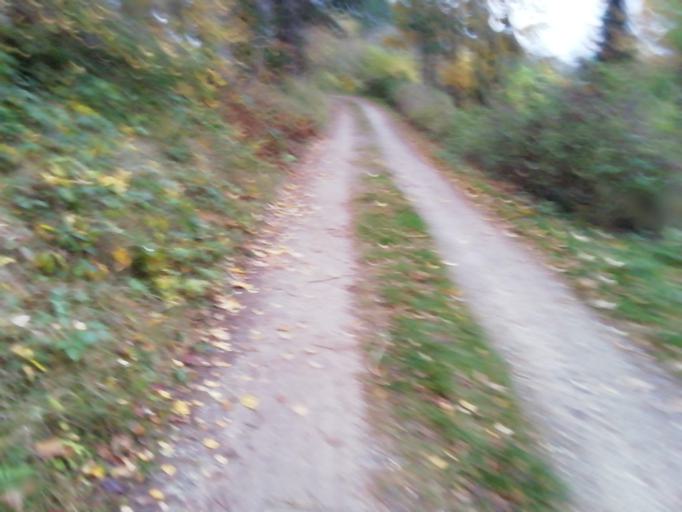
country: DK
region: Capital Region
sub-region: Frederikssund Kommune
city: Jaegerspris
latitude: 55.9035
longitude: 11.9264
